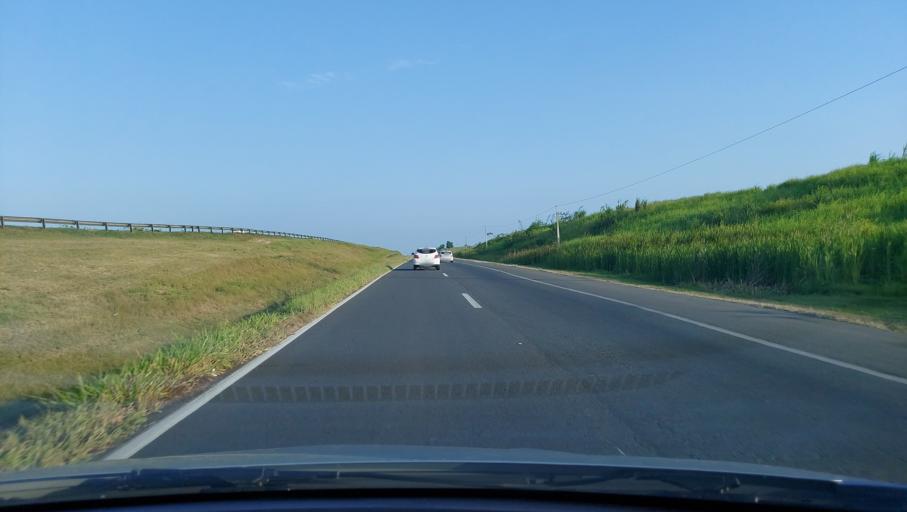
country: BR
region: Bahia
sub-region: Santo Amaro
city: Santo Amaro
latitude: -12.5065
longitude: -38.6346
